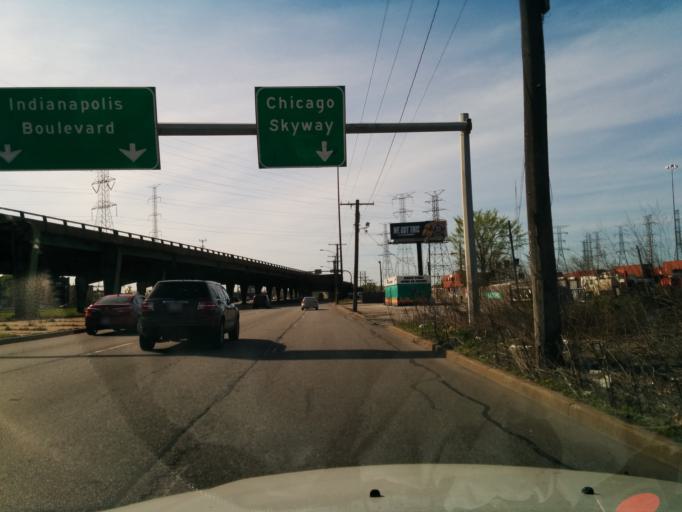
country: US
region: Indiana
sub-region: Lake County
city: Whiting
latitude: 41.7008
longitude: -87.5221
